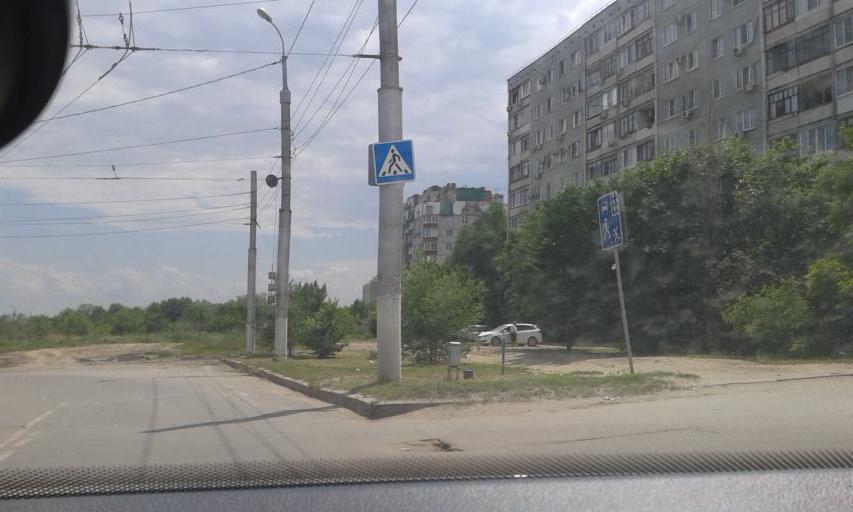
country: RU
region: Volgograd
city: Volgograd
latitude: 48.7558
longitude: 44.5113
